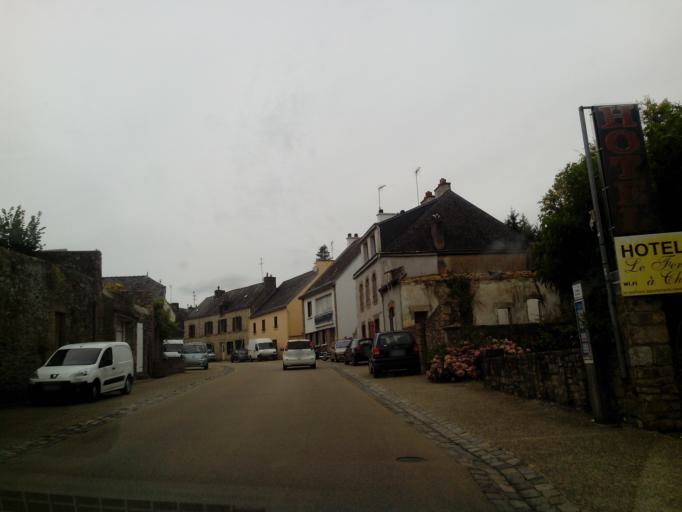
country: FR
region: Brittany
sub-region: Departement du Morbihan
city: Pont-Scorff
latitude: 47.8359
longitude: -3.3977
